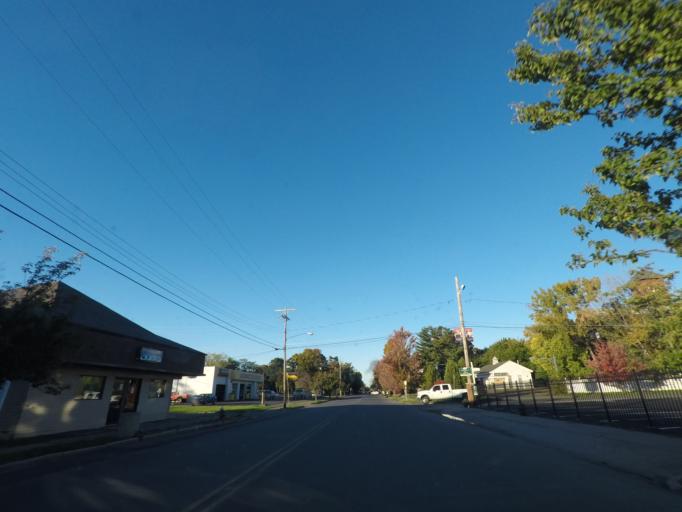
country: US
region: New York
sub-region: Albany County
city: Cohoes
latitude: 42.7670
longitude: -73.6807
